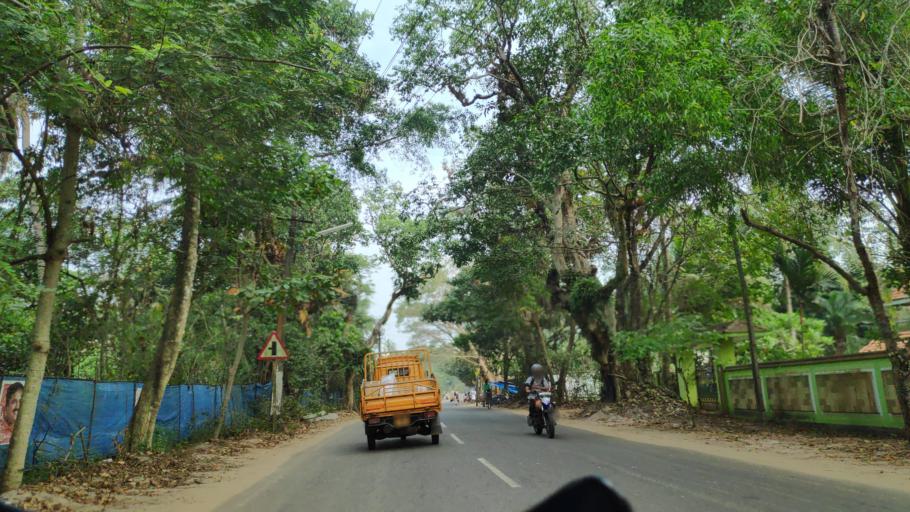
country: IN
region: Kerala
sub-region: Alappuzha
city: Vayalar
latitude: 9.7238
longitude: 76.3607
